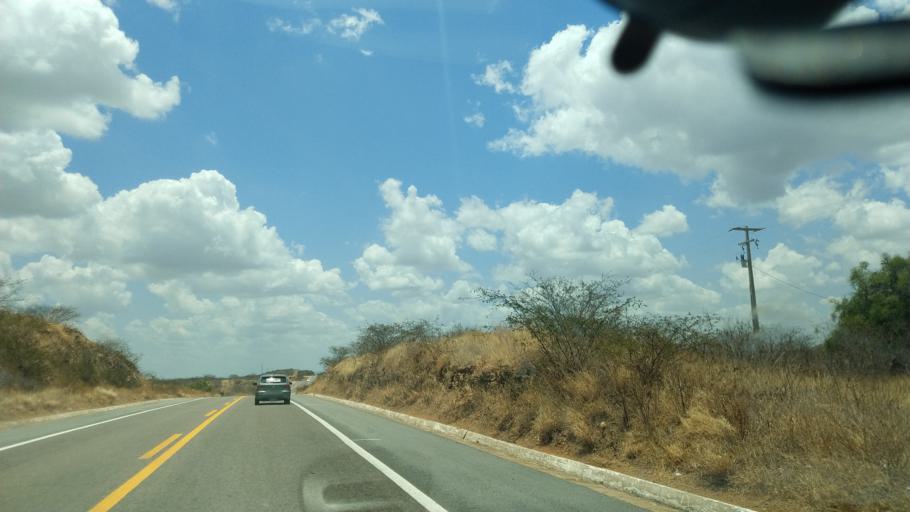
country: BR
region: Rio Grande do Norte
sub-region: Cerro Cora
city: Cerro Cora
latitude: -6.2085
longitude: -36.3129
